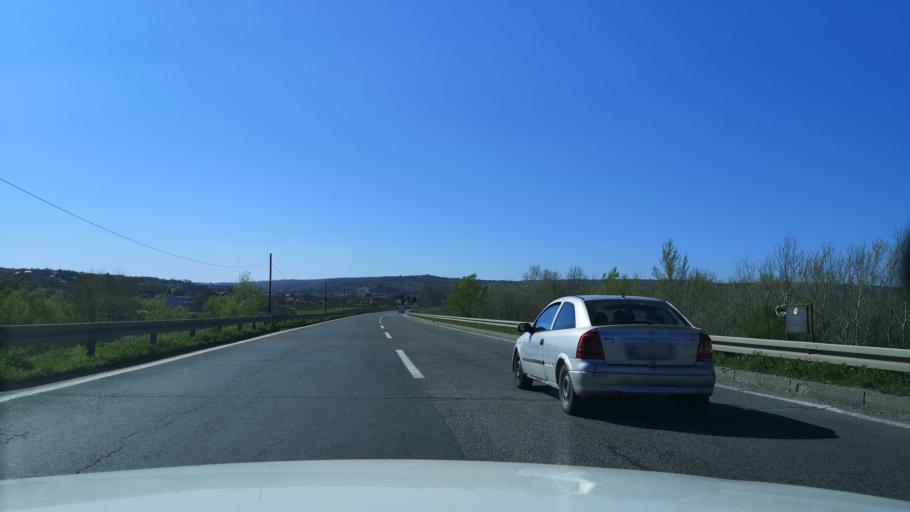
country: RS
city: Ostruznica
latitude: 44.7067
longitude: 20.3181
